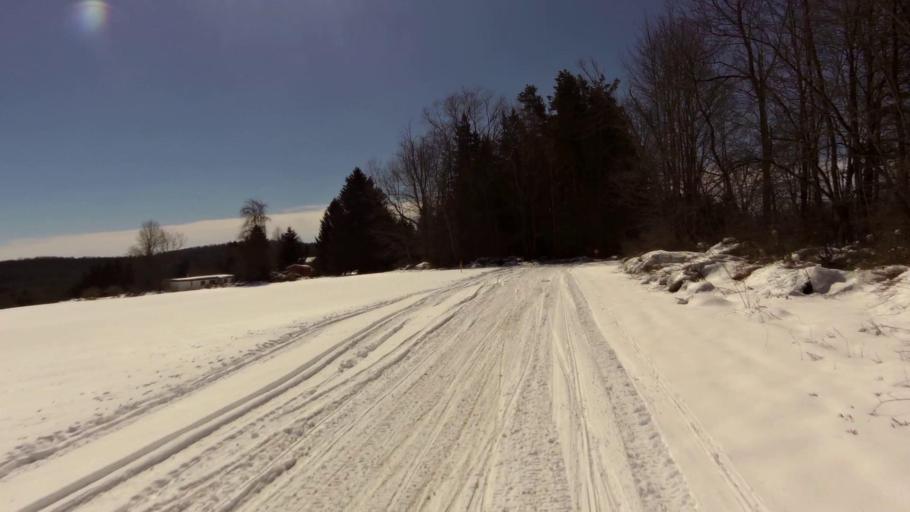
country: US
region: New York
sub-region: Allegany County
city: Houghton
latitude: 42.3607
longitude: -78.1579
